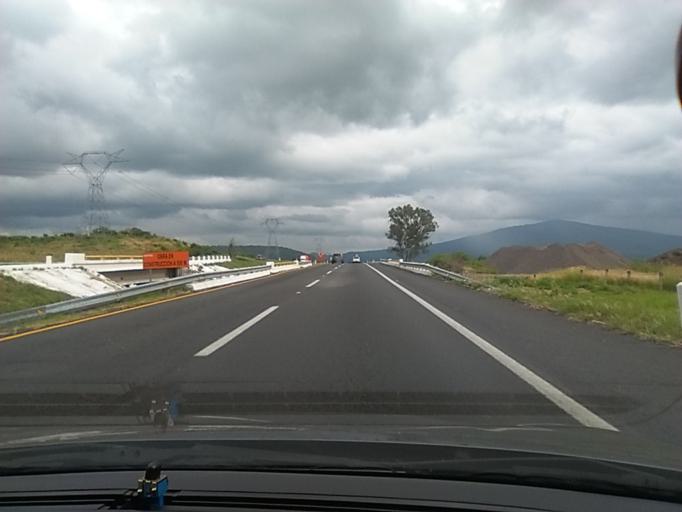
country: MX
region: Jalisco
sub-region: Zapotlanejo
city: La Mezquitera
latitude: 20.5913
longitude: -103.1056
